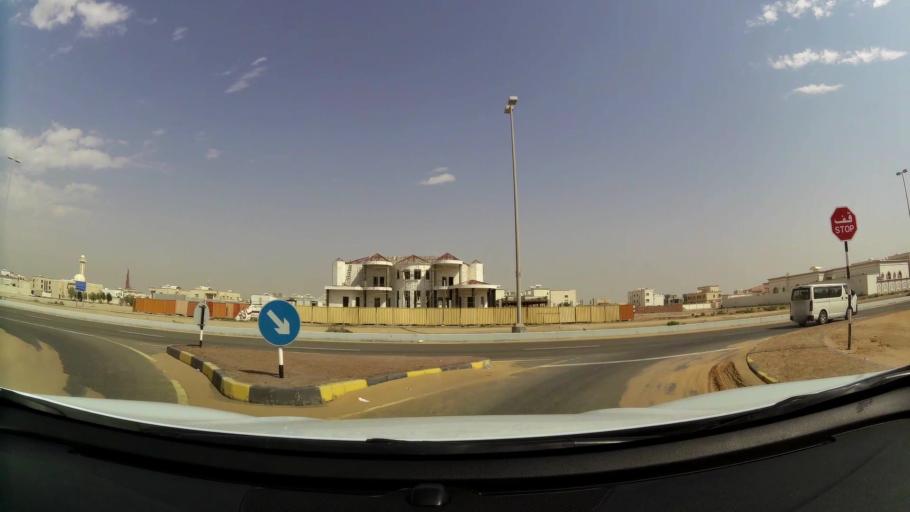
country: AE
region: Abu Dhabi
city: Abu Dhabi
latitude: 24.3353
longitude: 54.5485
